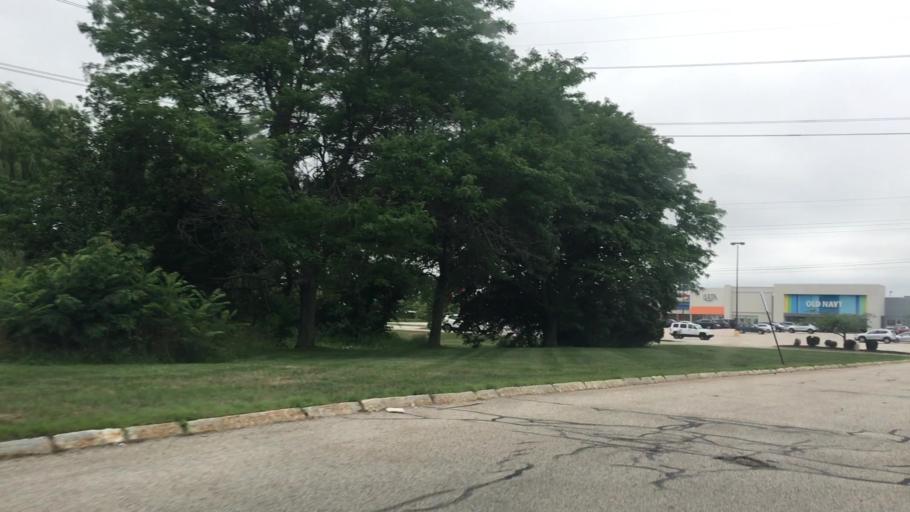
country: US
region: Maine
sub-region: York County
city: South Eliot
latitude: 43.0928
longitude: -70.7980
